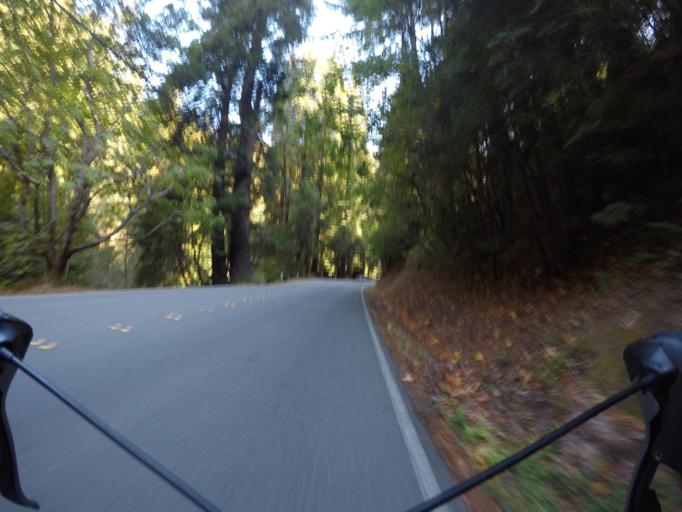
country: US
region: California
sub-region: San Mateo County
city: Portola Valley
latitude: 37.2693
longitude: -122.3165
